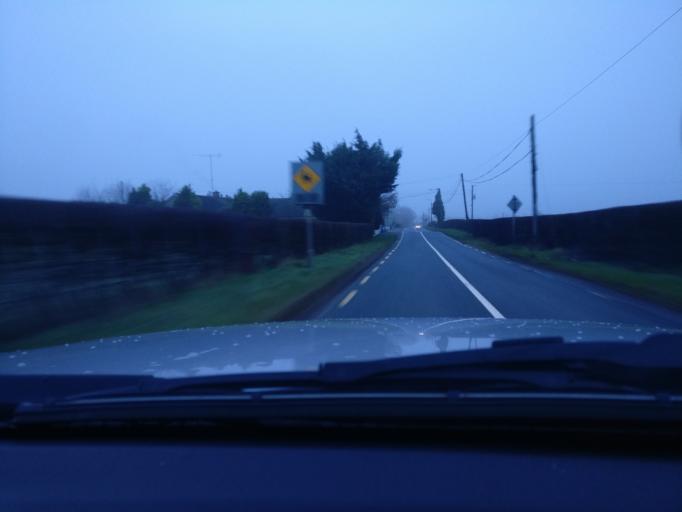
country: IE
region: Leinster
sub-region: An Mhi
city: Ballivor
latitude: 53.6109
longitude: -7.0387
